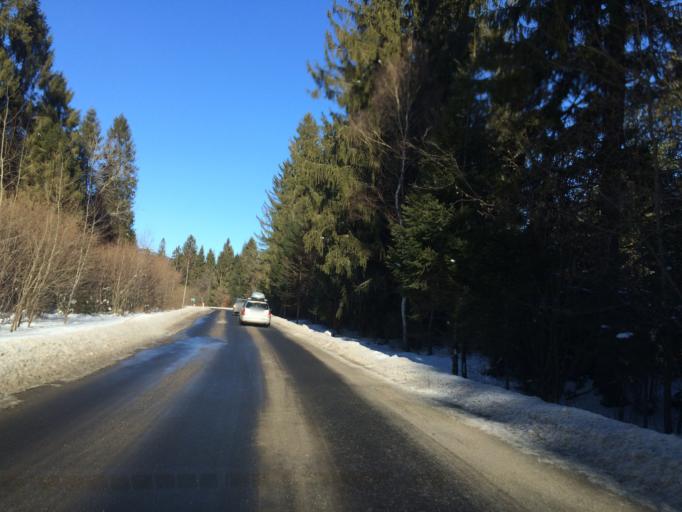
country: PL
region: Subcarpathian Voivodeship
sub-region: Powiat leski
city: Cisna
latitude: 49.1690
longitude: 22.4475
